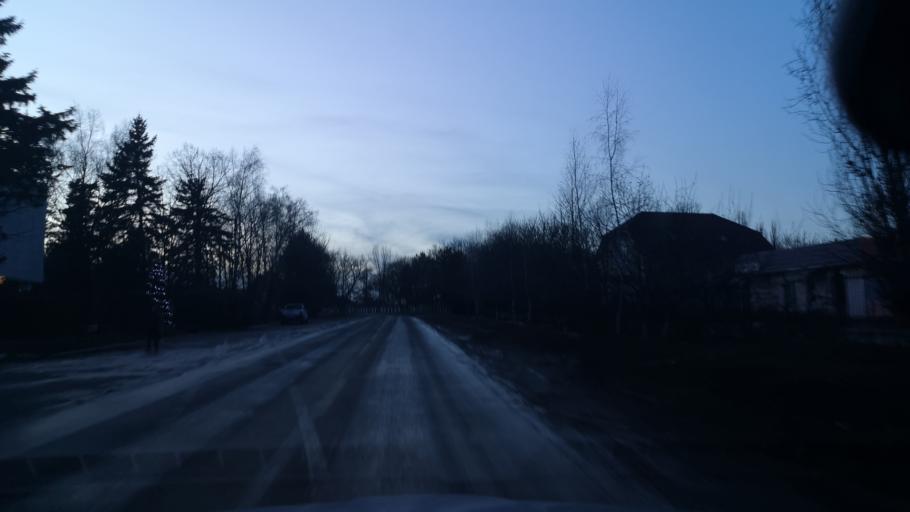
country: MD
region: Orhei
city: Orhei
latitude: 47.2877
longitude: 28.8589
